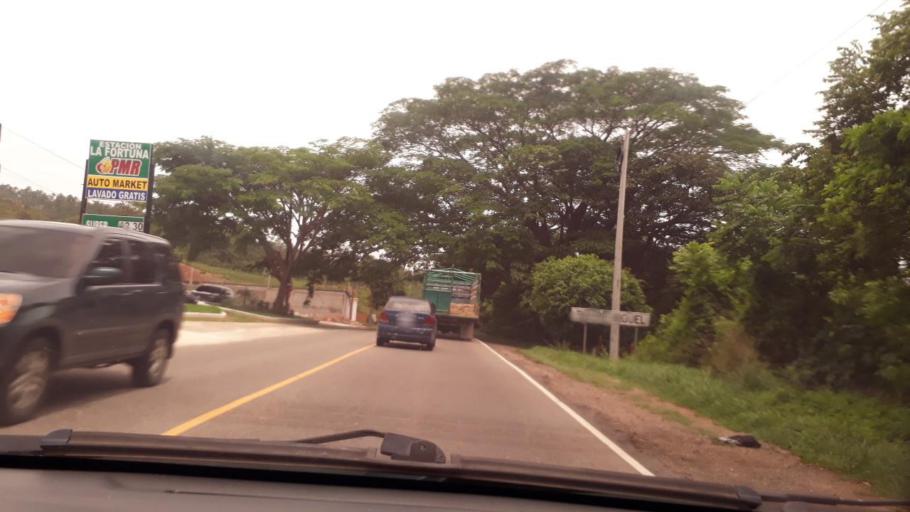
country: GT
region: Chiquimula
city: Concepcion Las Minas
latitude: 14.5666
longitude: -89.4496
